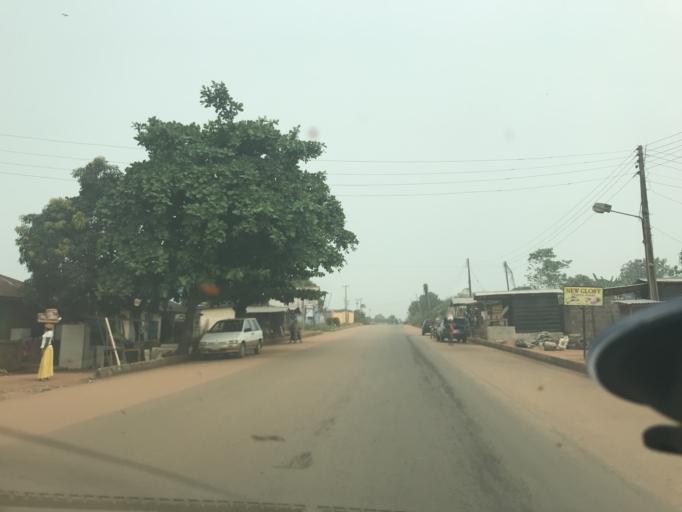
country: NG
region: Ogun
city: Ilaro
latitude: 6.8936
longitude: 3.0177
